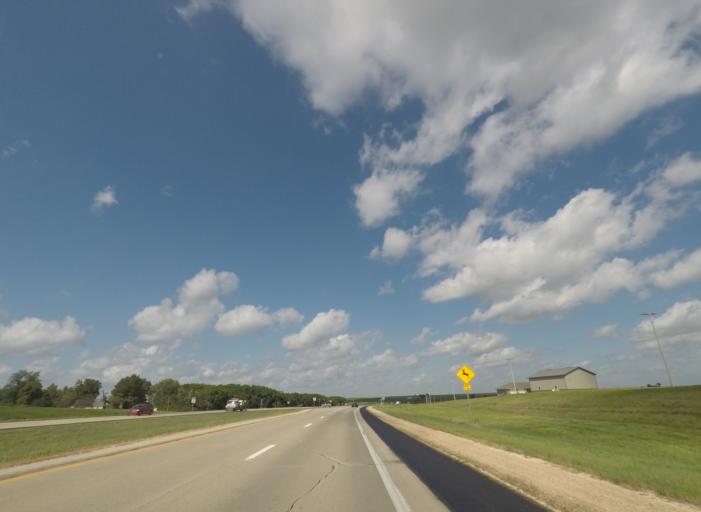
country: US
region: Iowa
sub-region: Jones County
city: Monticello
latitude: 42.2731
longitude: -91.1400
